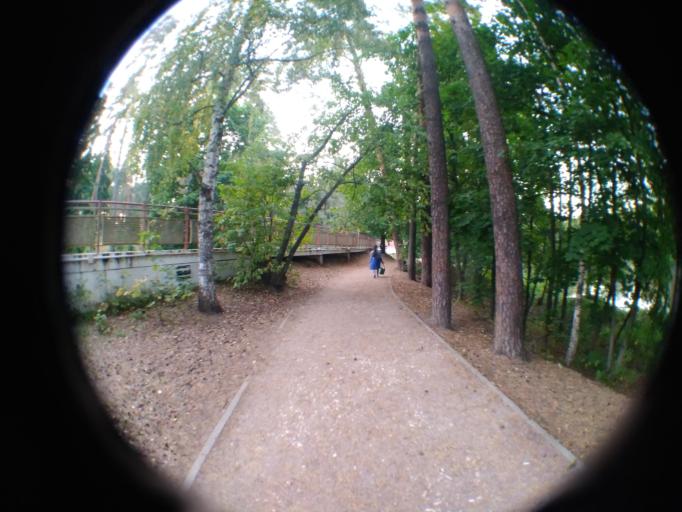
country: RU
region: Moskovskaya
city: Kratovo
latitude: 55.5881
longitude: 38.1580
